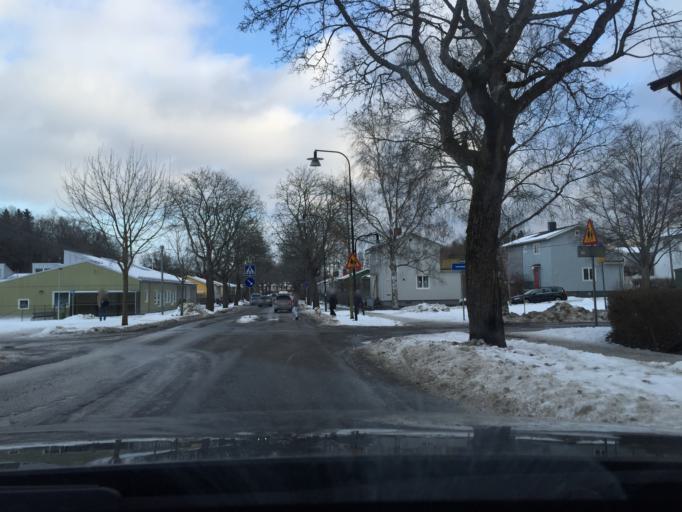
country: SE
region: Stockholm
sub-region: Stockholms Kommun
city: Bromma
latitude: 59.3459
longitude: 17.9151
